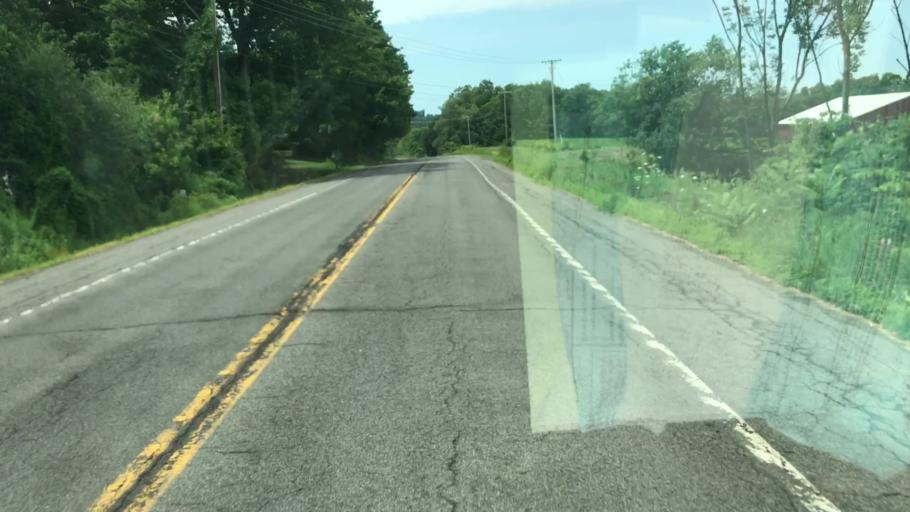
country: US
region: New York
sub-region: Onondaga County
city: Nedrow
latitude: 42.9119
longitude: -76.2261
